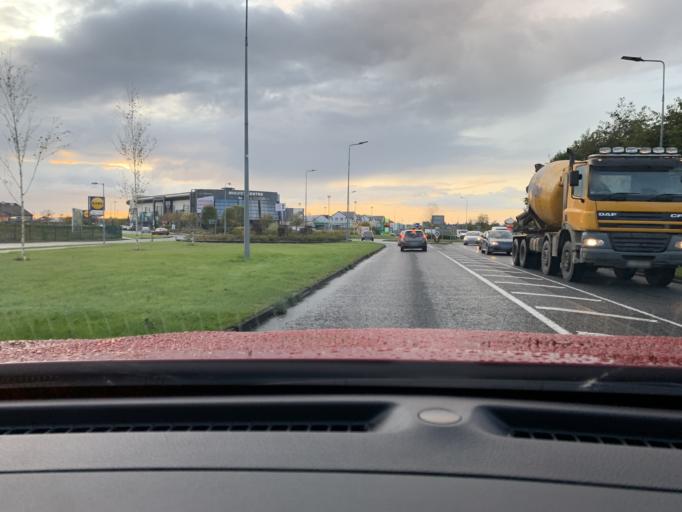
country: IE
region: Connaught
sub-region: County Leitrim
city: Carrick-on-Shannon
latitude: 53.9417
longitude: -8.1031
